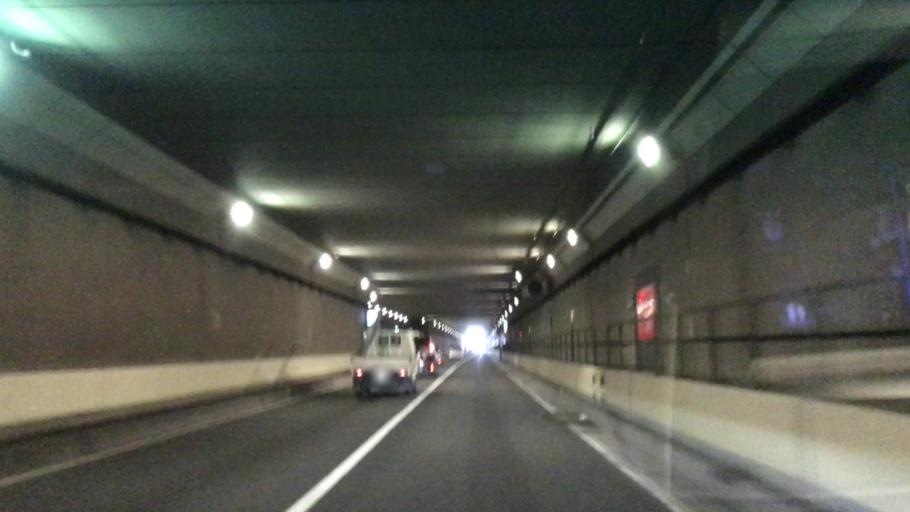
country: JP
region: Hokkaido
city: Sapporo
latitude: 43.0587
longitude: 141.3577
